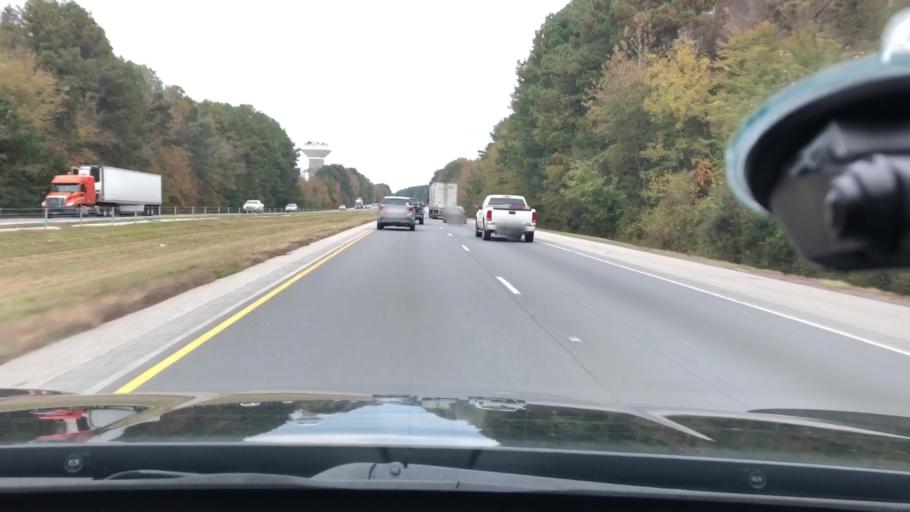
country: US
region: Arkansas
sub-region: Clark County
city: Arkadelphia
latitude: 34.1286
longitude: -93.0874
